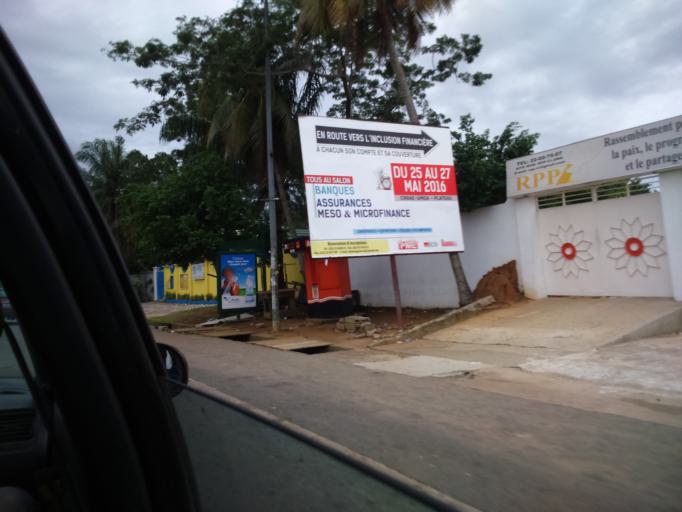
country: CI
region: Lagunes
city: Abidjan
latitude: 5.3524
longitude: -3.9914
